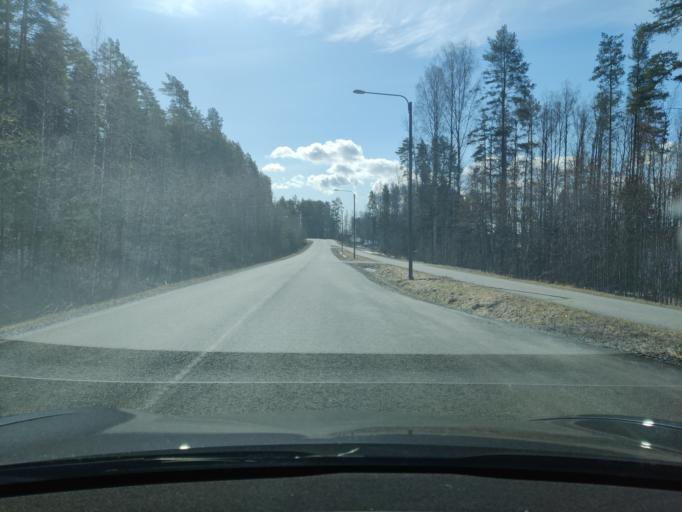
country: FI
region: Northern Savo
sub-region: Kuopio
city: Vehmersalmi
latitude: 62.7689
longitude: 28.0103
